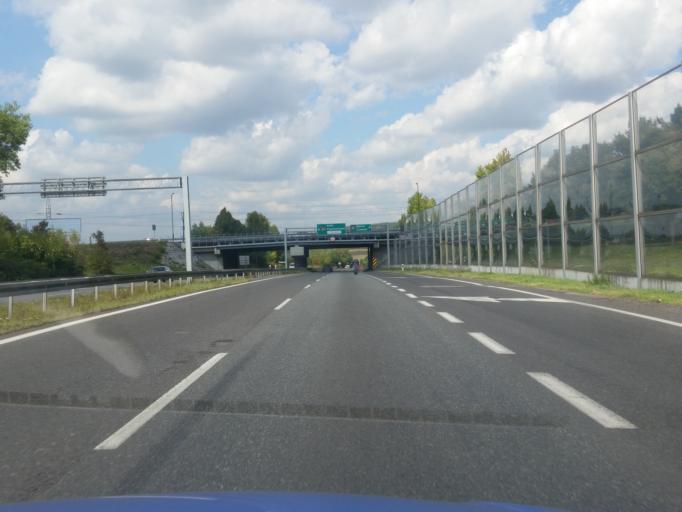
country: PL
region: Silesian Voivodeship
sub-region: Powiat bedzinski
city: Bedzin
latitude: 50.3217
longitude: 19.1074
